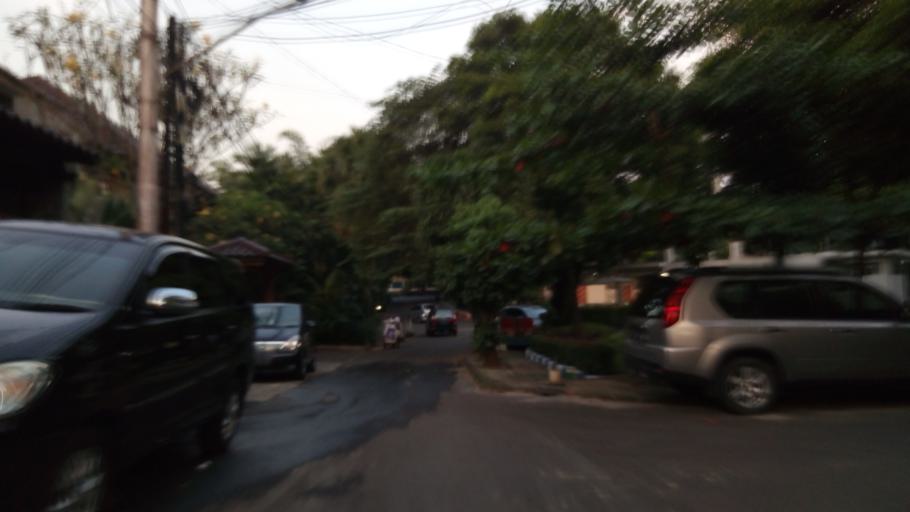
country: ID
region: Jakarta Raya
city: Jakarta
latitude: -6.2421
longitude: 106.7945
